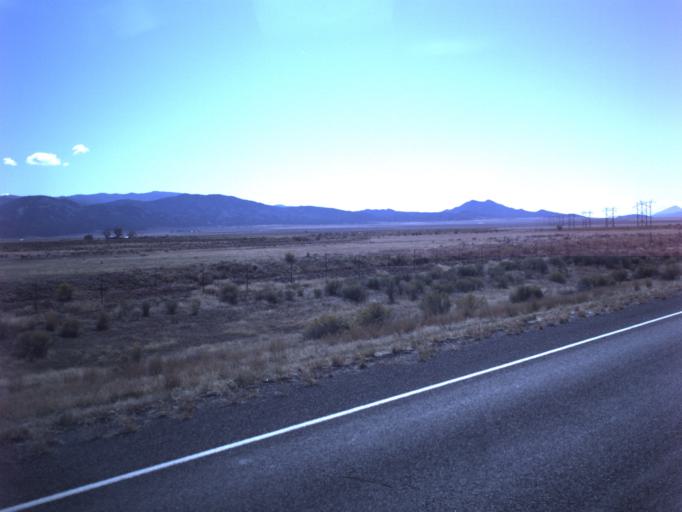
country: US
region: Utah
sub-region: Juab County
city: Nephi
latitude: 39.5341
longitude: -111.9311
